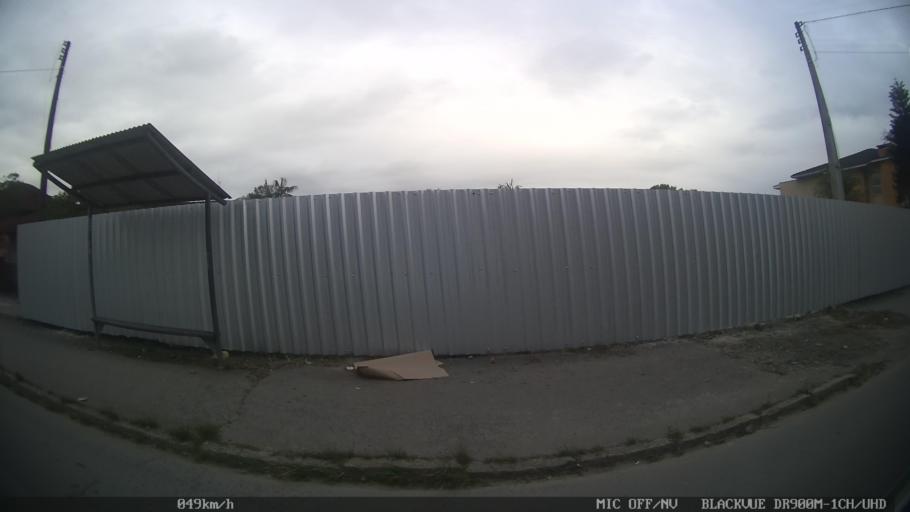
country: BR
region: Santa Catarina
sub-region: Joinville
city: Joinville
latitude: -26.2854
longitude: -48.8706
